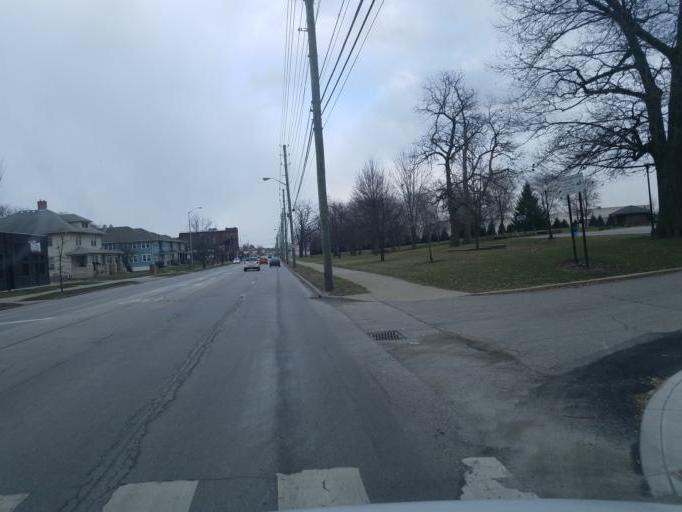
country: US
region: Indiana
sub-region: Marion County
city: Indianapolis
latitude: 39.7674
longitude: -86.1284
